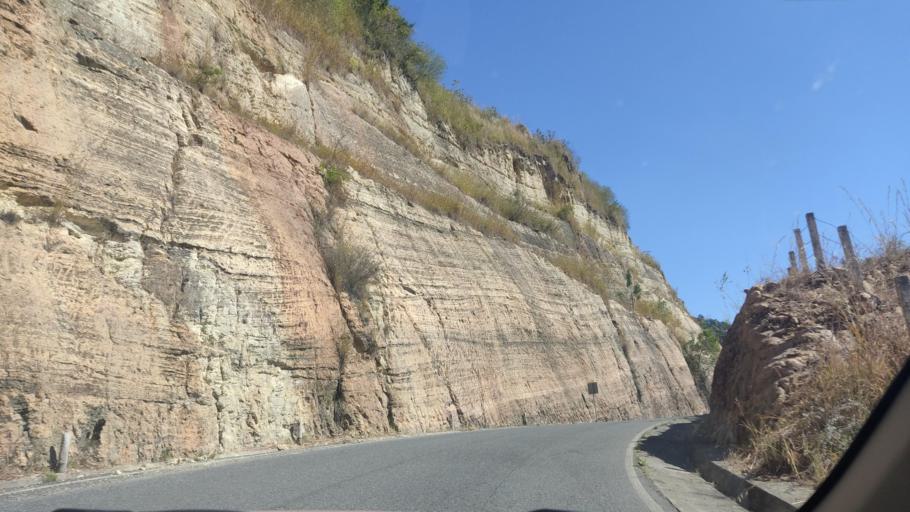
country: MX
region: Nayarit
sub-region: Jala
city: Rosa Blanca
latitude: 21.0920
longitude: -104.3812
